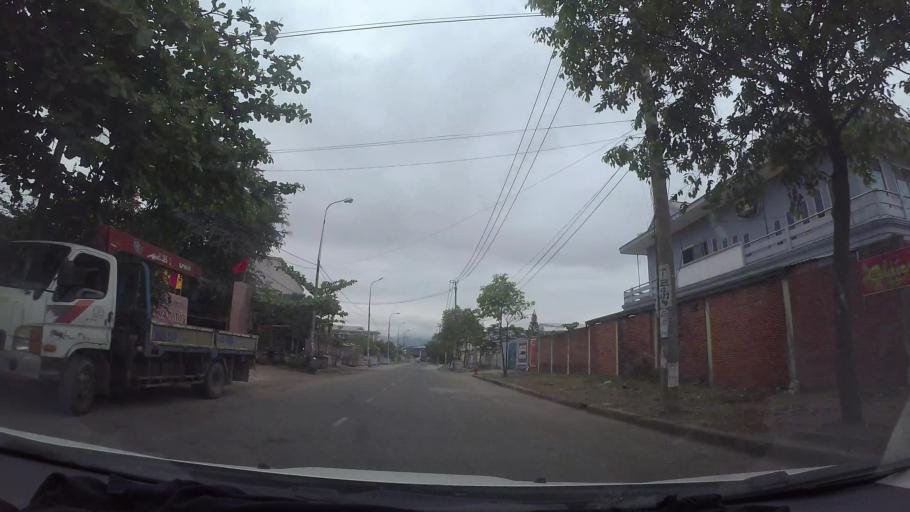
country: VN
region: Da Nang
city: Lien Chieu
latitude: 16.0855
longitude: 108.1386
